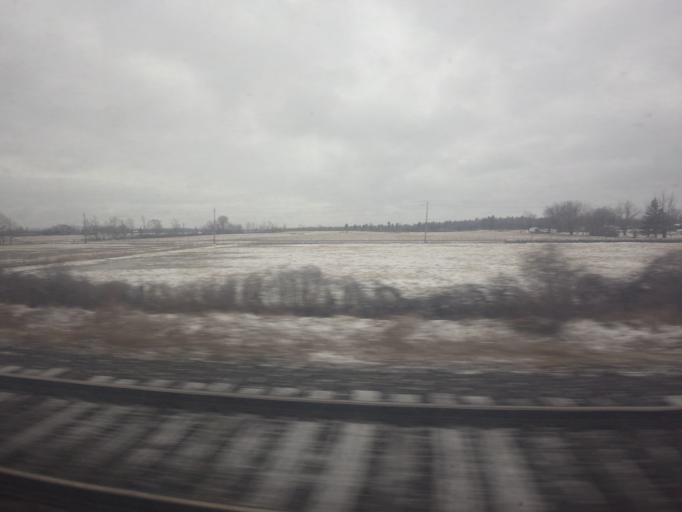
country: CA
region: Ontario
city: Gananoque
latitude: 44.3697
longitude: -76.1458
